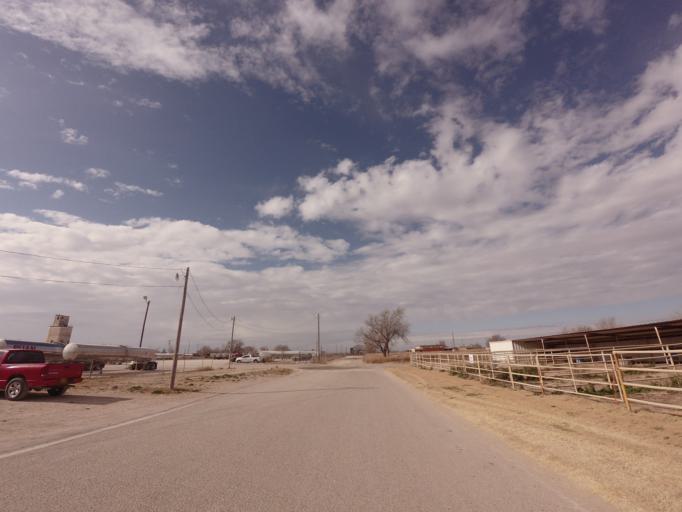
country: US
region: New Mexico
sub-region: Curry County
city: Clovis
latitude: 34.3928
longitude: -103.2175
